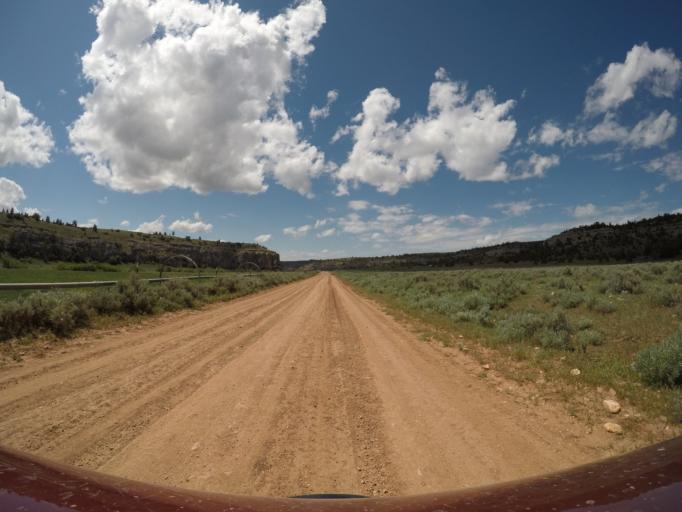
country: US
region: Montana
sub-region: Yellowstone County
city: Laurel
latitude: 45.2402
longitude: -108.6347
